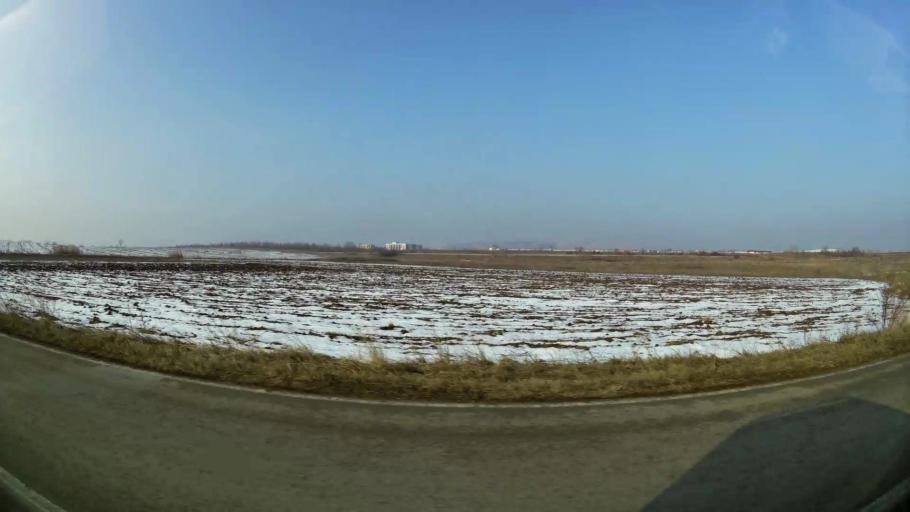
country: MK
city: Kadino
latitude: 41.9792
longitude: 21.6149
